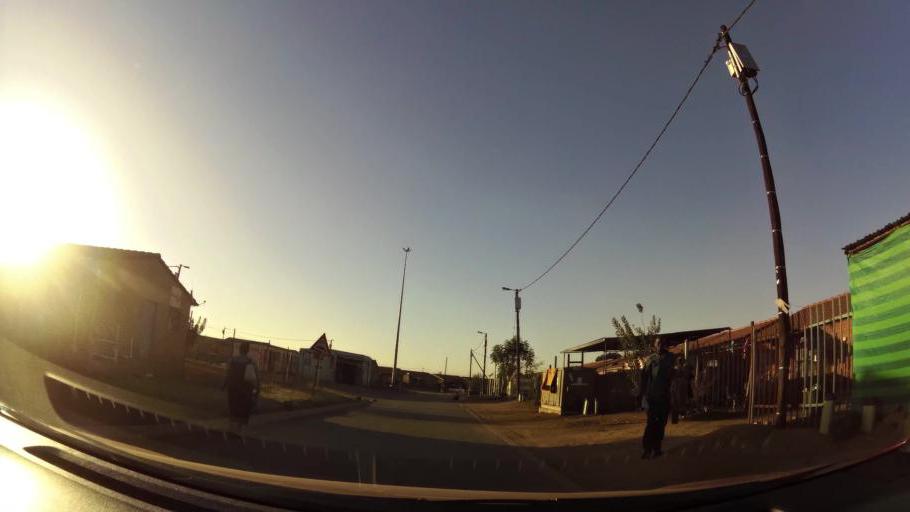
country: ZA
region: Gauteng
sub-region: City of Tshwane Metropolitan Municipality
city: Mabopane
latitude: -25.6038
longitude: 28.1097
